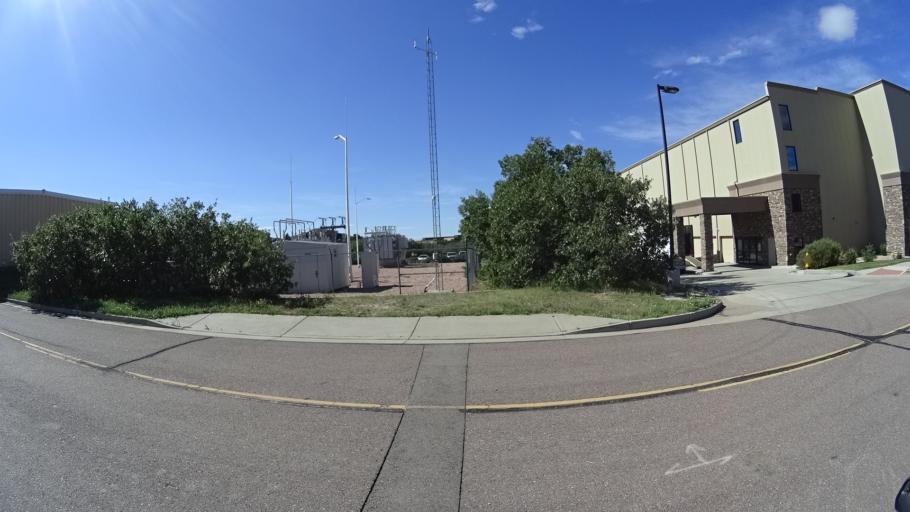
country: US
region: Colorado
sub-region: El Paso County
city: Gleneagle
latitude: 39.0213
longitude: -104.8115
